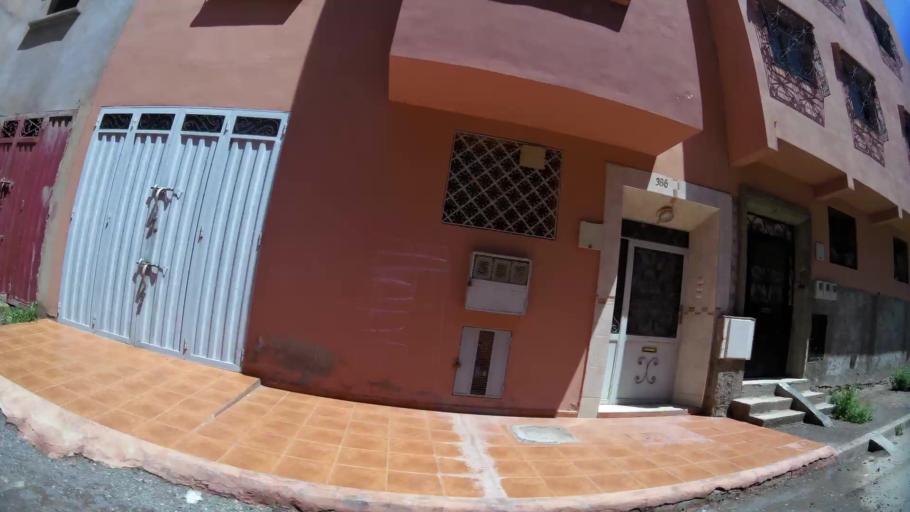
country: MA
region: Marrakech-Tensift-Al Haouz
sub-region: Marrakech
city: Marrakesh
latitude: 31.6413
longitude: -8.0498
